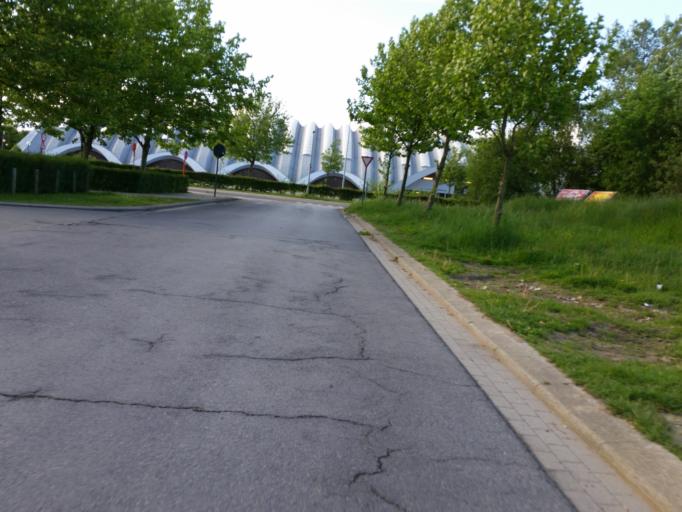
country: BE
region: Flanders
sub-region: Provincie Antwerpen
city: Mechelen
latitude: 51.0261
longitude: 4.4992
